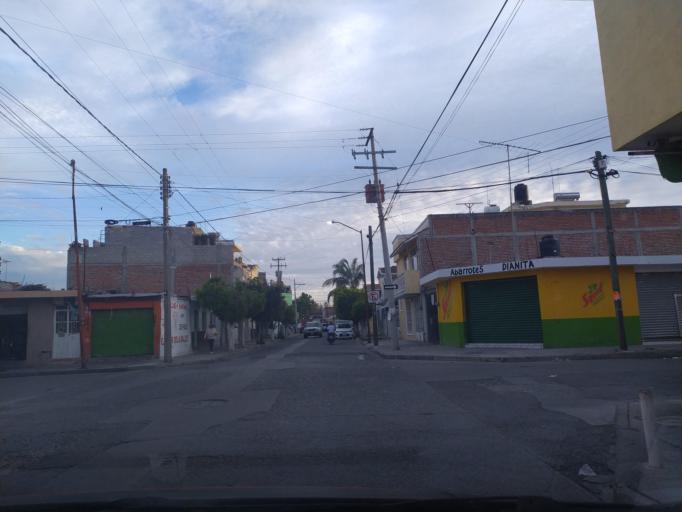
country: LA
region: Oudomxai
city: Muang La
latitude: 21.0180
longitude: 101.8657
